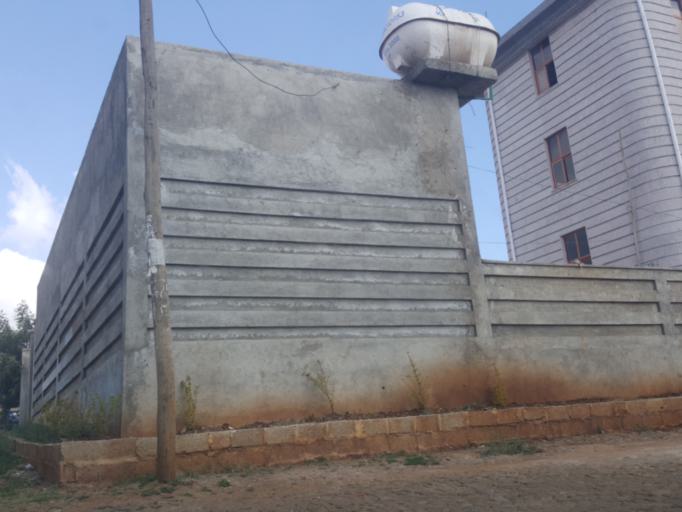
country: ET
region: Adis Abeba
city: Addis Ababa
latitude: 9.0682
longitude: 38.7174
